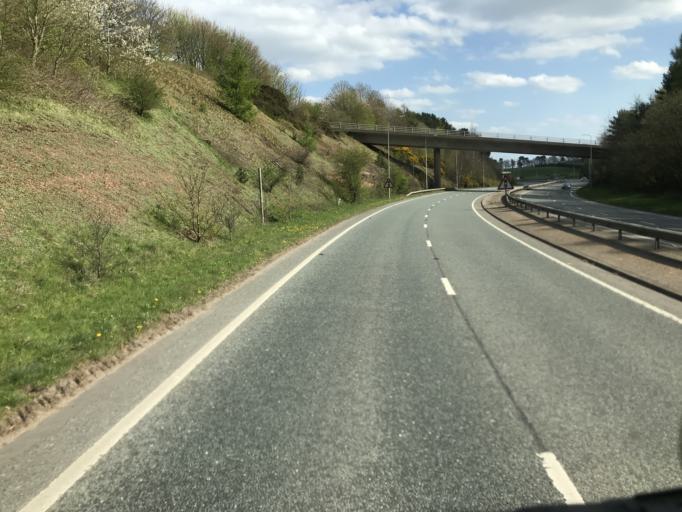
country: GB
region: England
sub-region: Cheshire West and Chester
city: Kelsall
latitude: 53.2152
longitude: -2.7024
